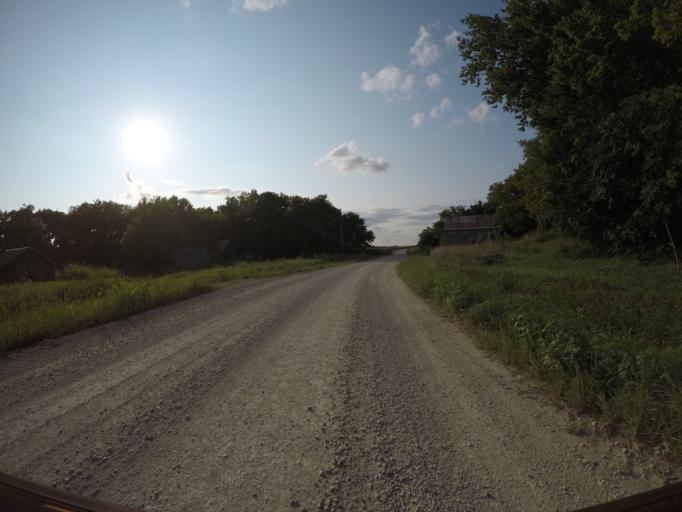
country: US
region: Kansas
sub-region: Wabaunsee County
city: Alma
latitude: 38.9258
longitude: -96.2265
